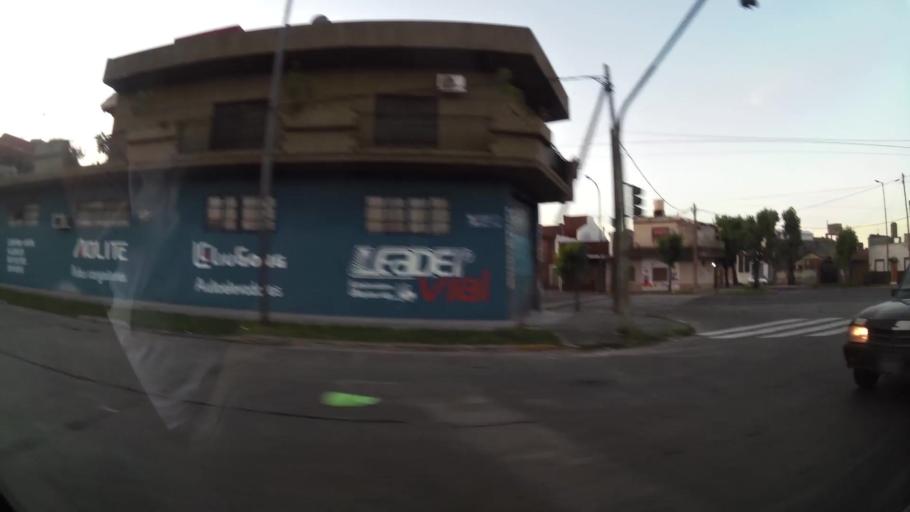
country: AR
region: Buenos Aires F.D.
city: Villa Lugano
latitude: -34.6725
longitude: -58.4703
